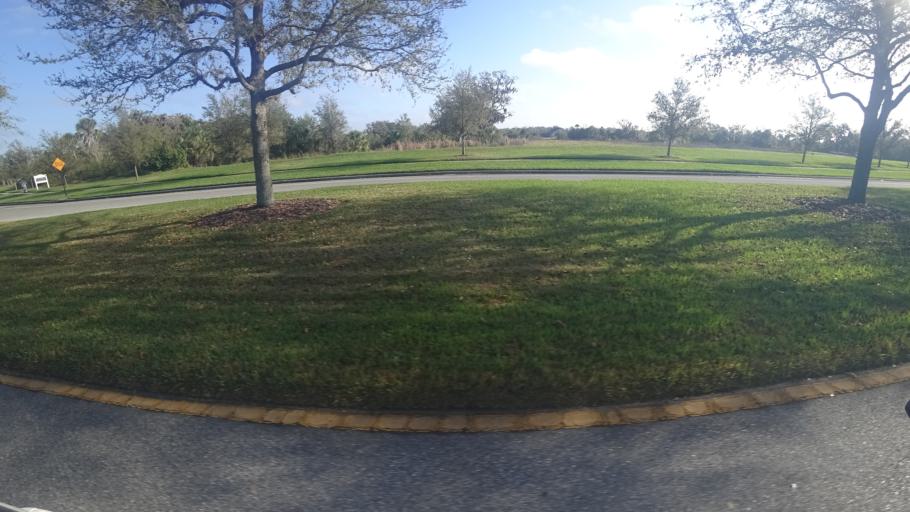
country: US
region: Florida
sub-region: Manatee County
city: Ellenton
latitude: 27.5580
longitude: -82.4576
